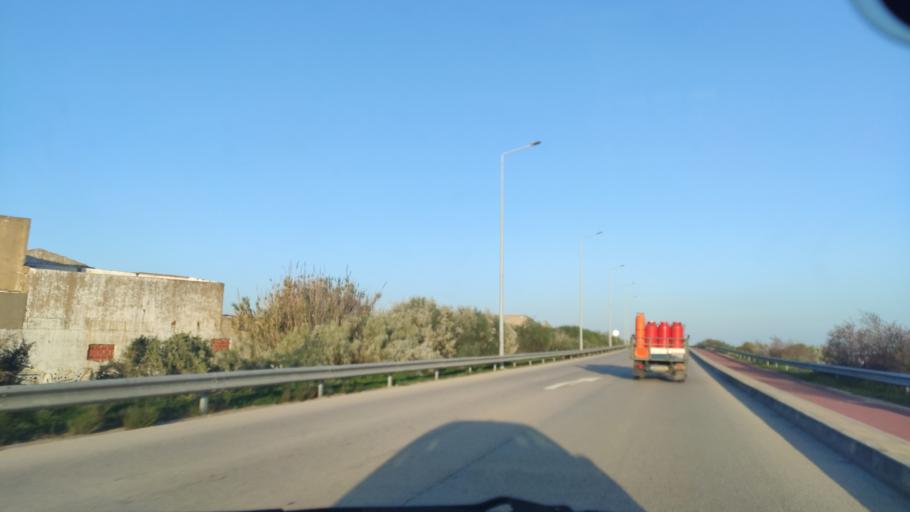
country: PT
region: Faro
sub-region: Faro
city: Faro
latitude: 37.0108
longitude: -7.9207
